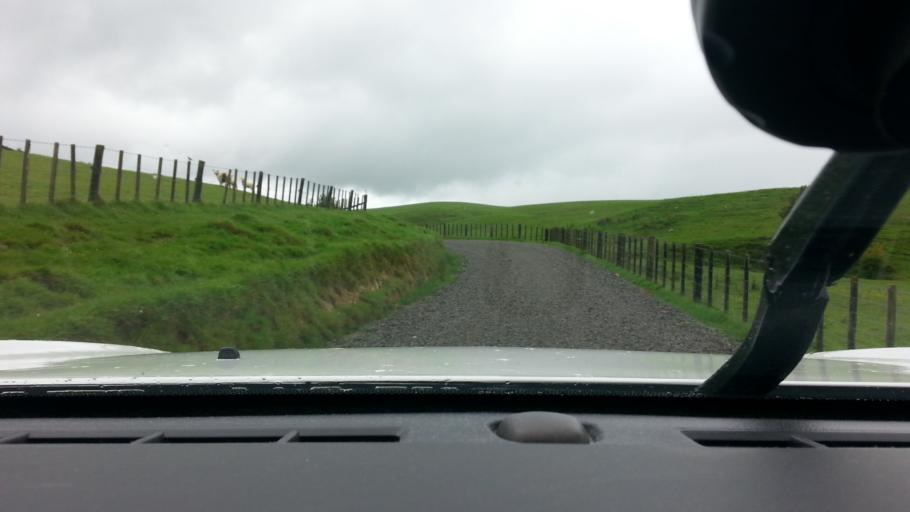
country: NZ
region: Wellington
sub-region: Masterton District
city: Masterton
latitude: -40.9244
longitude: 175.5409
